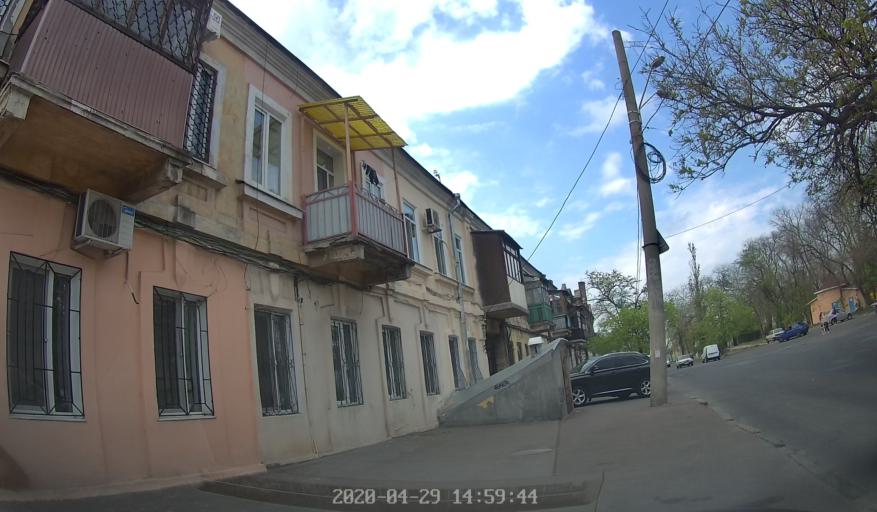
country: NG
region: Niger
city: Lemu
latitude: 9.2977
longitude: 6.1435
